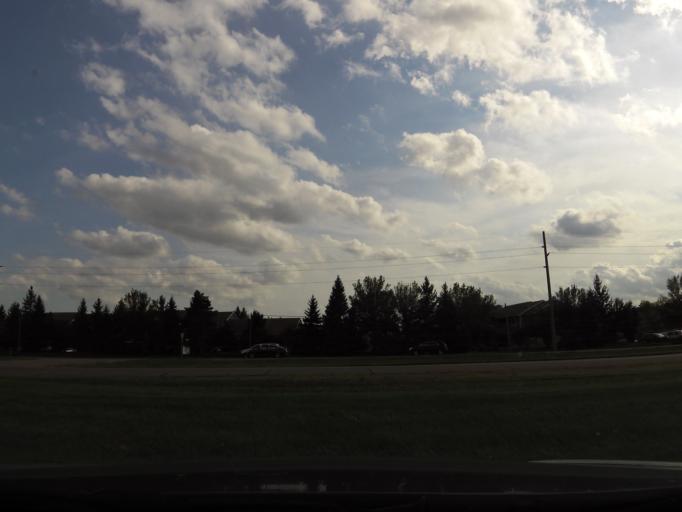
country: US
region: Minnesota
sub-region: Dakota County
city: Burnsville
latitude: 44.7384
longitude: -93.2616
